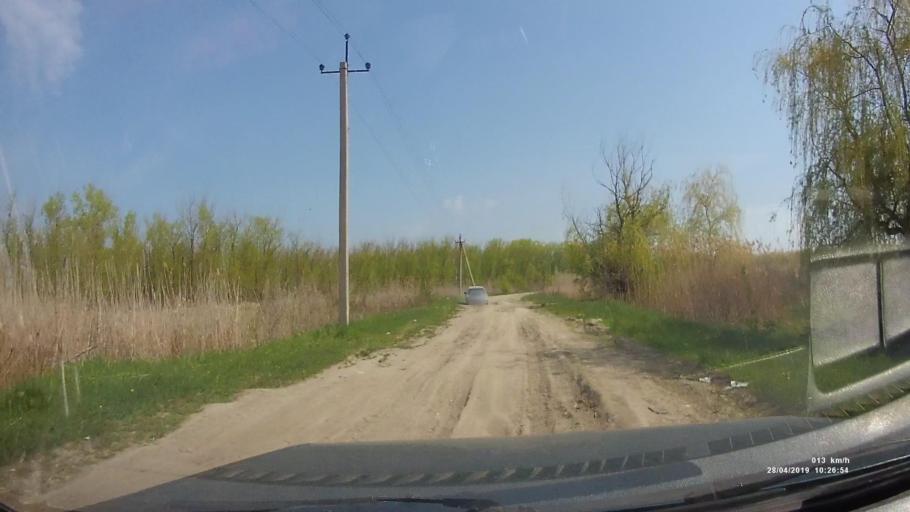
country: RU
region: Rostov
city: Azov
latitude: 47.1140
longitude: 39.4447
